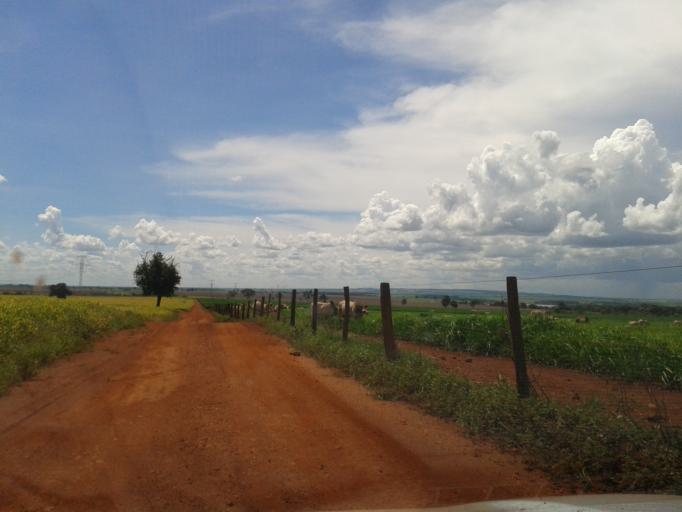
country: BR
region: Minas Gerais
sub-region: Capinopolis
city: Capinopolis
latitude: -18.7024
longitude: -49.7837
